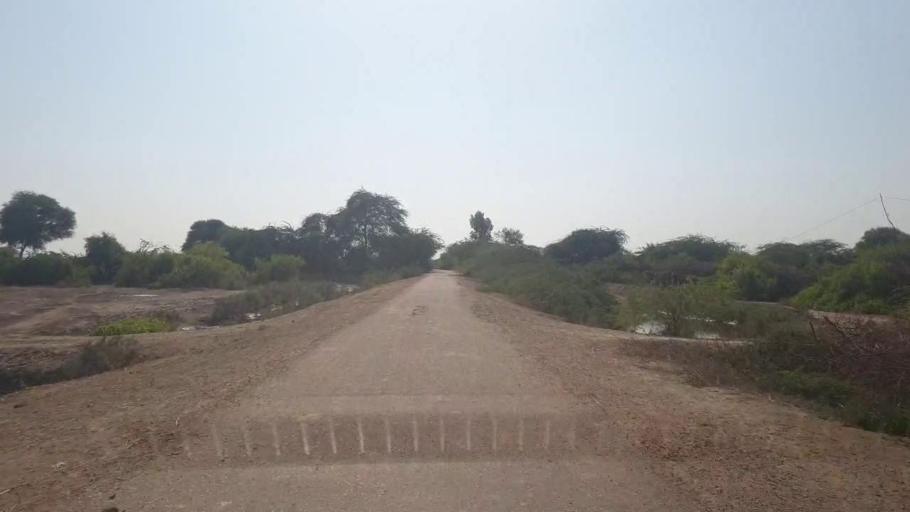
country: PK
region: Sindh
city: Badin
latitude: 24.5510
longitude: 68.8129
